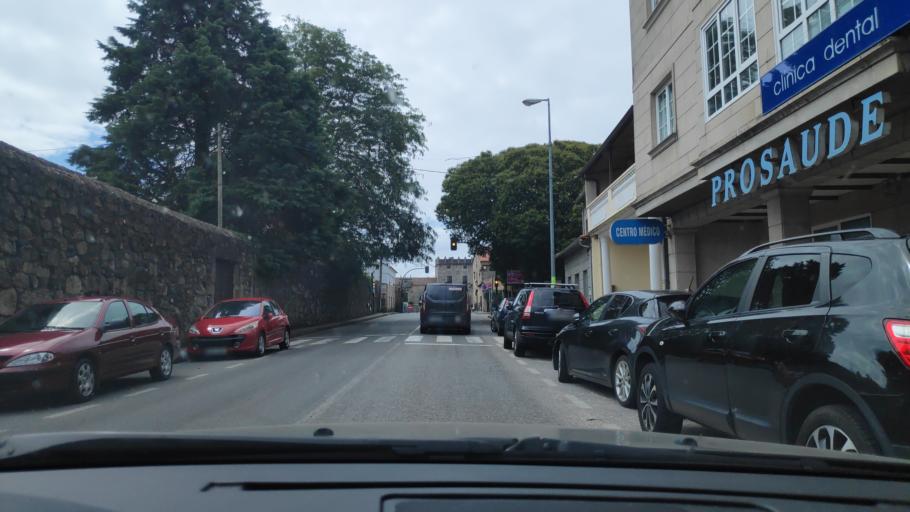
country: ES
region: Galicia
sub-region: Provincia de Pontevedra
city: Cambados
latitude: 42.5205
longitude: -8.8132
